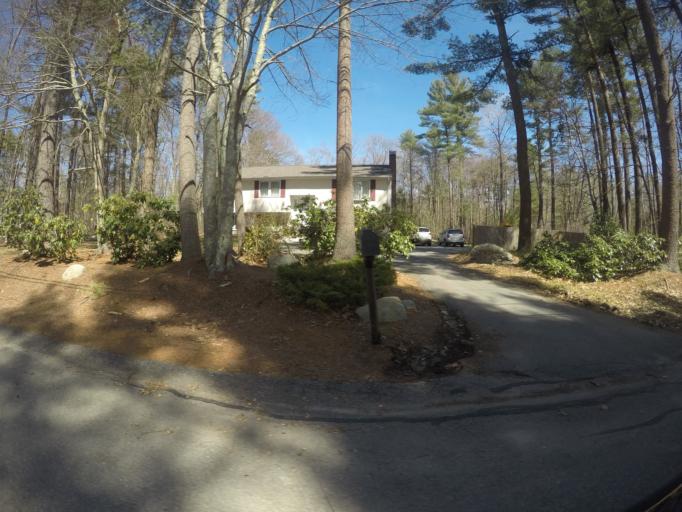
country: US
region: Massachusetts
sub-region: Bristol County
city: Easton
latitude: 42.0321
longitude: -71.0935
